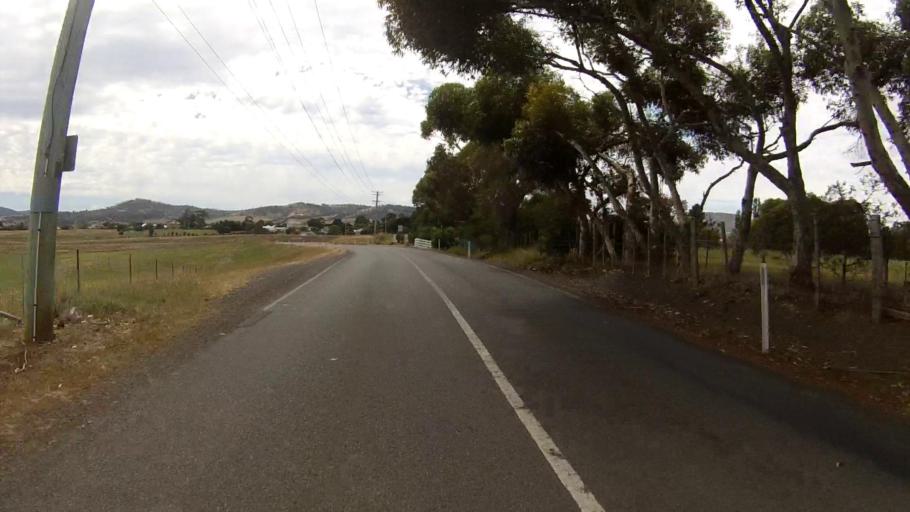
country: AU
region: Tasmania
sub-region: Clarence
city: Cambridge
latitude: -42.7379
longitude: 147.4272
